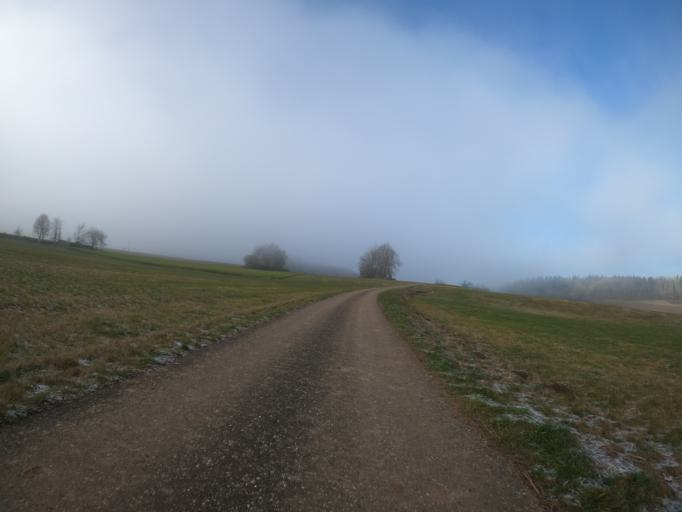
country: DE
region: Baden-Wuerttemberg
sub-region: Regierungsbezirk Stuttgart
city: Deggingen
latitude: 48.5911
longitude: 9.7527
